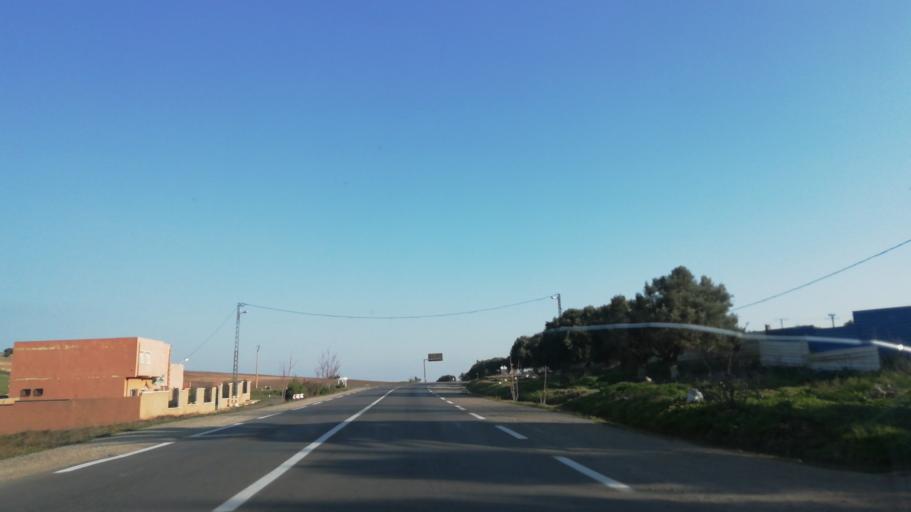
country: DZ
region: Ain Temouchent
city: Hammam Bou Hadjar
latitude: 35.1645
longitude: -0.8751
